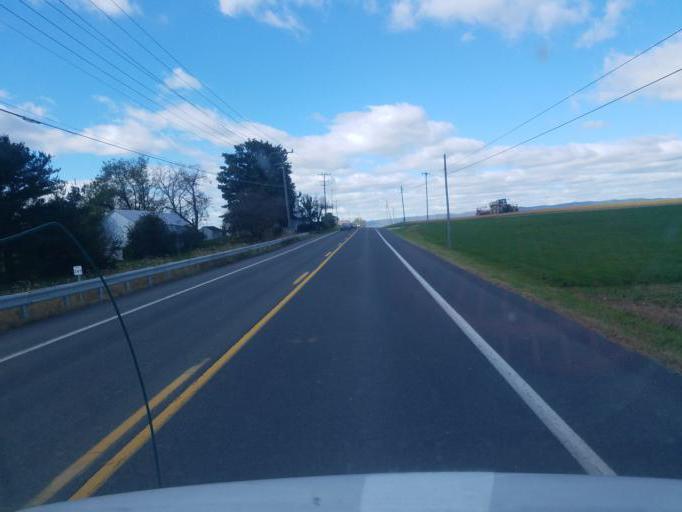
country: US
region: Pennsylvania
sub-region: Franklin County
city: Mercersburg
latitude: 39.8036
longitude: -77.8292
